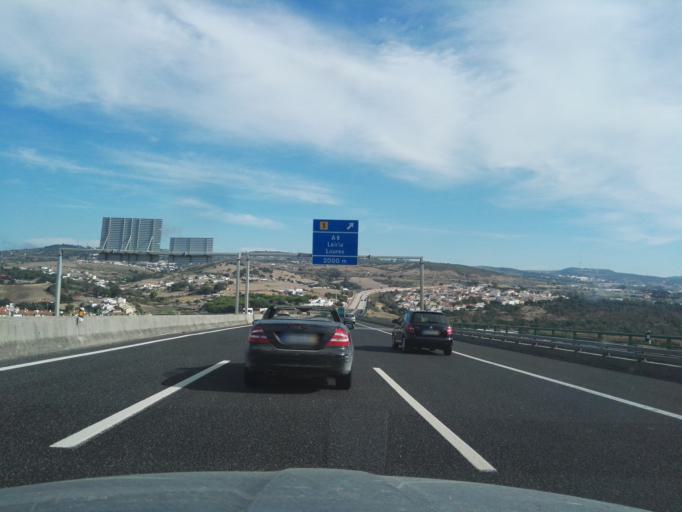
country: PT
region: Lisbon
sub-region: Loures
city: Loures
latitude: 38.8366
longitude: -9.1889
